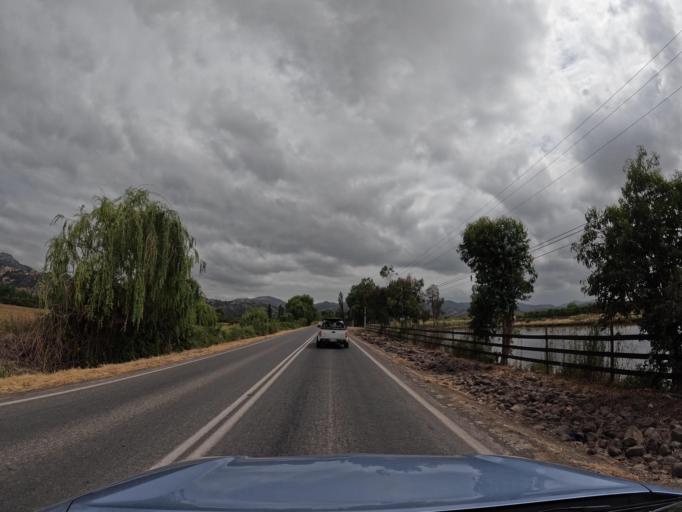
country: CL
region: Maule
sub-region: Provincia de Curico
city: Teno
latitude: -34.8440
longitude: -71.1867
